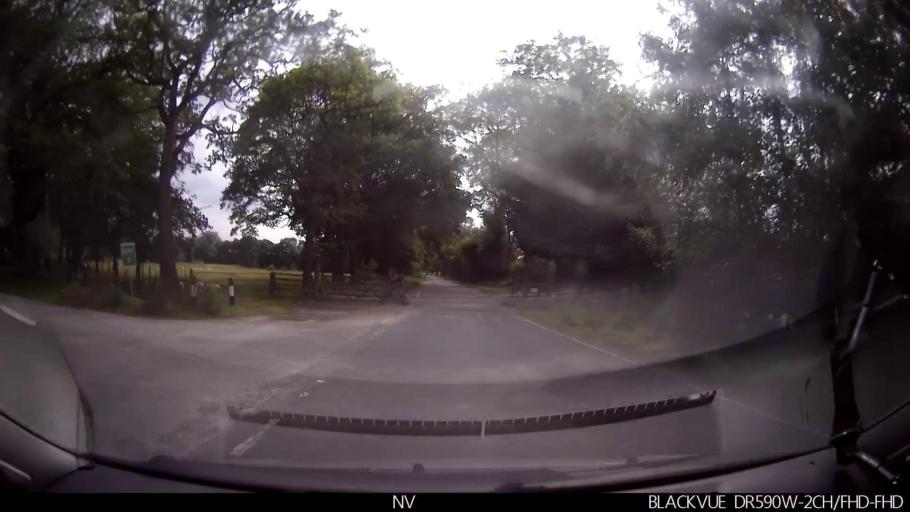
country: GB
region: England
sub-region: North Yorkshire
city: Strensall
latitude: 54.0428
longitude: -1.0114
